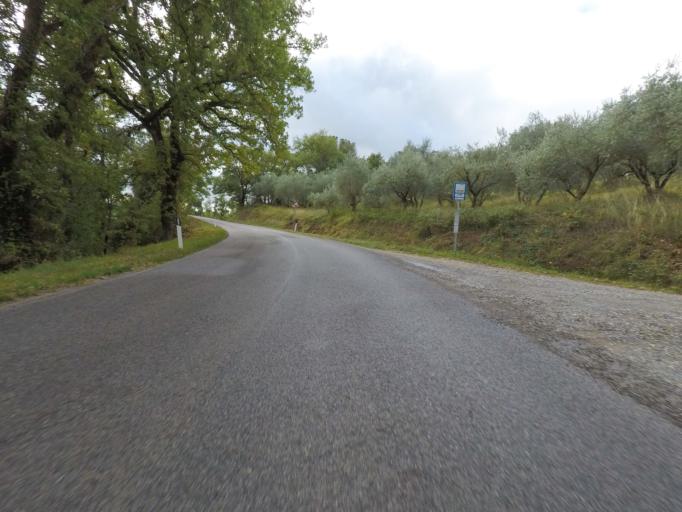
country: IT
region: Tuscany
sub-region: Provincia di Siena
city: Belverde
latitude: 43.4088
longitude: 11.3515
